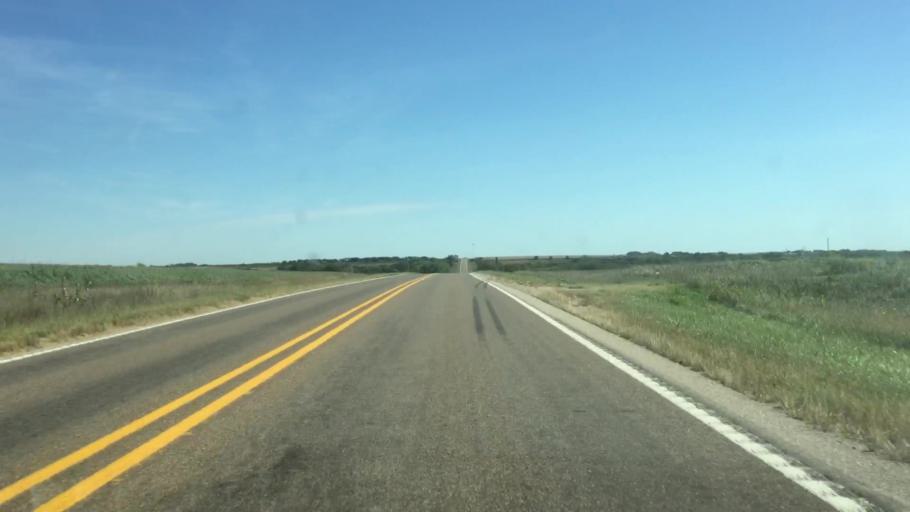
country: US
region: Nebraska
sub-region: Thayer County
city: Hebron
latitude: 40.1473
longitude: -97.5078
